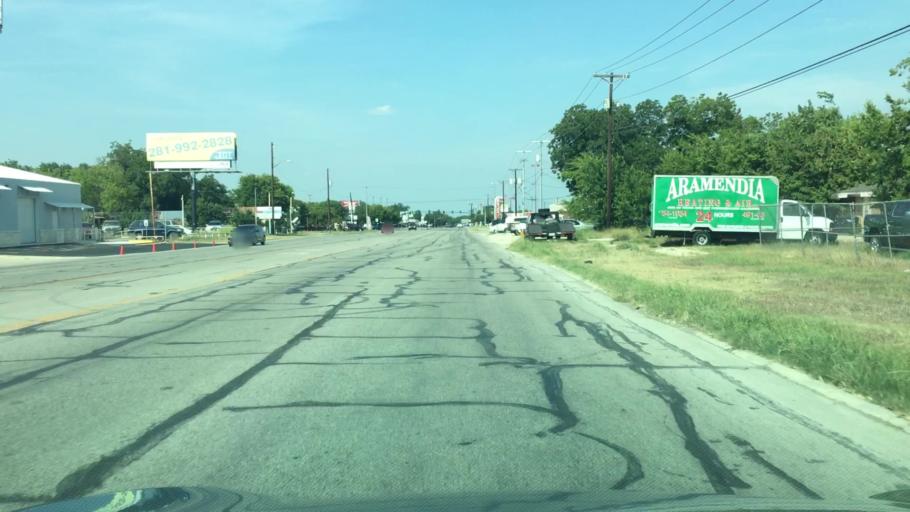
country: US
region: Texas
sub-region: Comal County
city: New Braunfels
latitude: 29.6876
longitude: -98.1308
